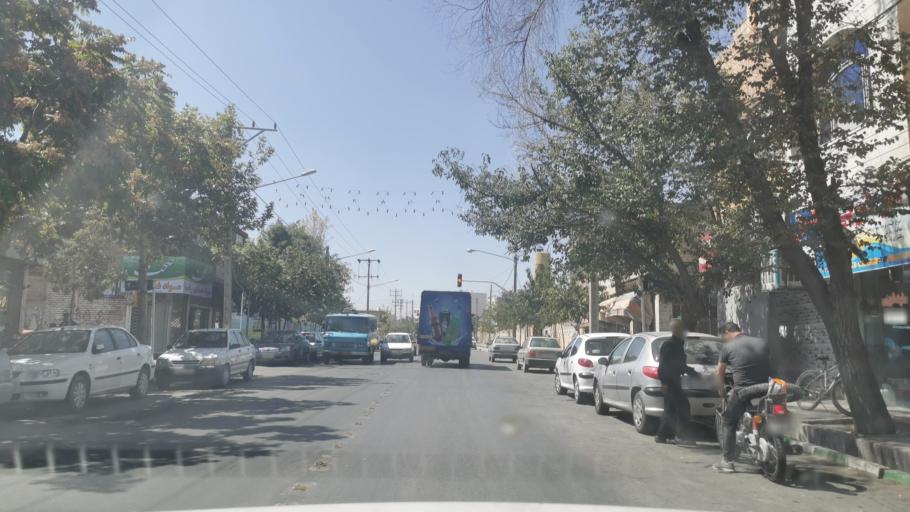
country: IR
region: Razavi Khorasan
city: Mashhad
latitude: 36.3582
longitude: 59.5445
